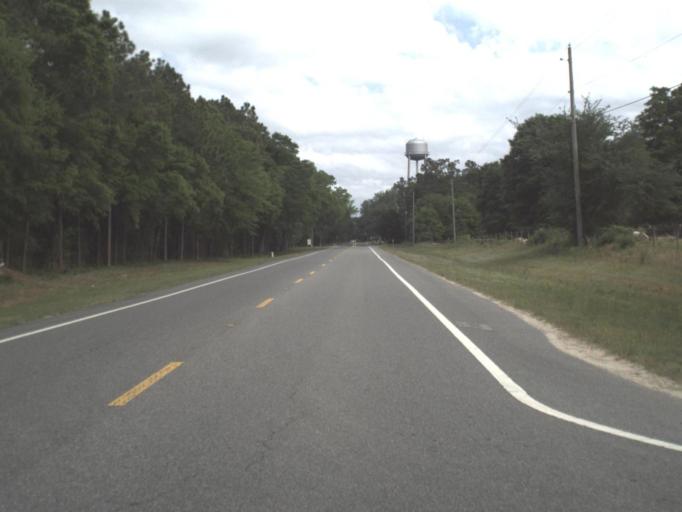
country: US
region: Florida
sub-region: Santa Rosa County
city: Point Baker
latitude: 30.6945
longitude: -87.0596
